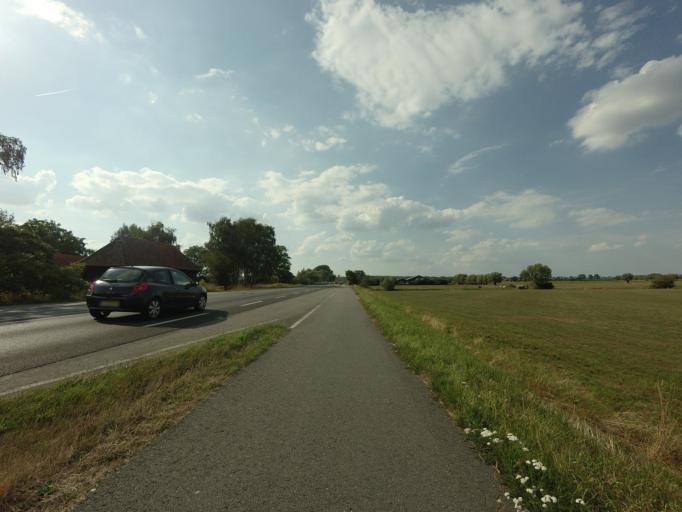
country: NL
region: Gelderland
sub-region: Gemeente Doesburg
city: Doesburg
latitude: 52.0236
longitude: 6.1196
